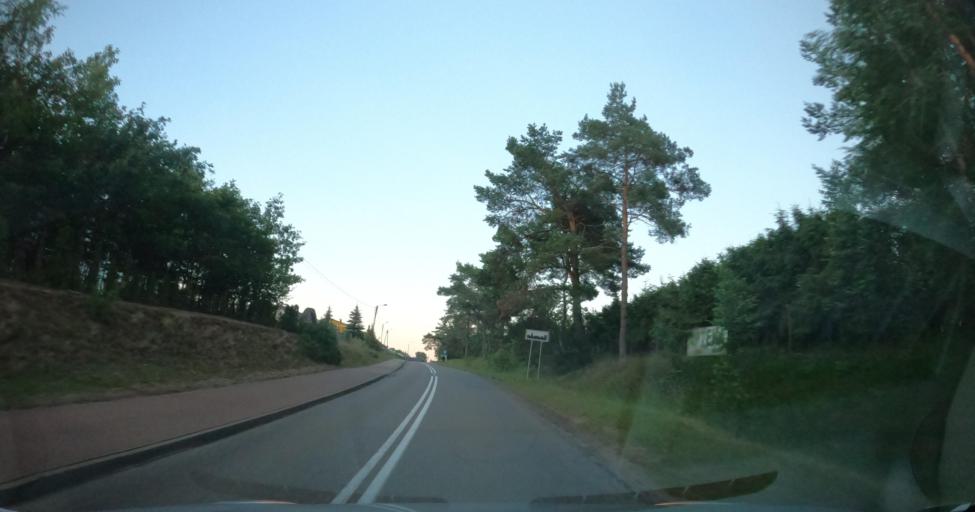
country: PL
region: Pomeranian Voivodeship
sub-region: Powiat wejherowski
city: Linia
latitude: 54.4572
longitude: 18.0112
